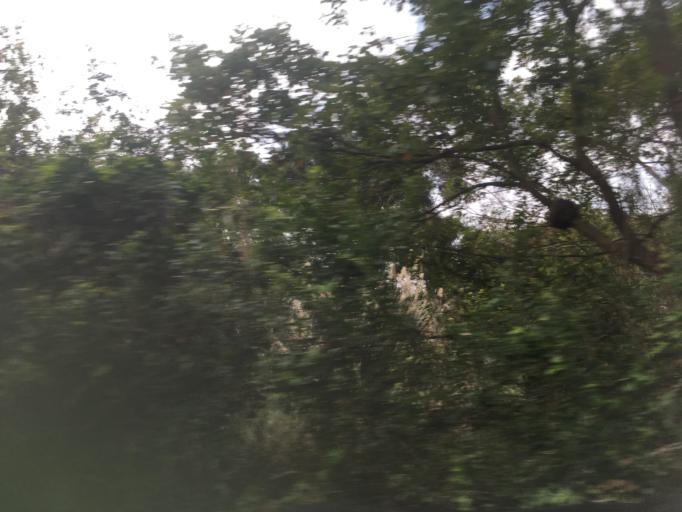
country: TW
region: Taiwan
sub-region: Miaoli
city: Miaoli
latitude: 24.4421
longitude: 120.7064
